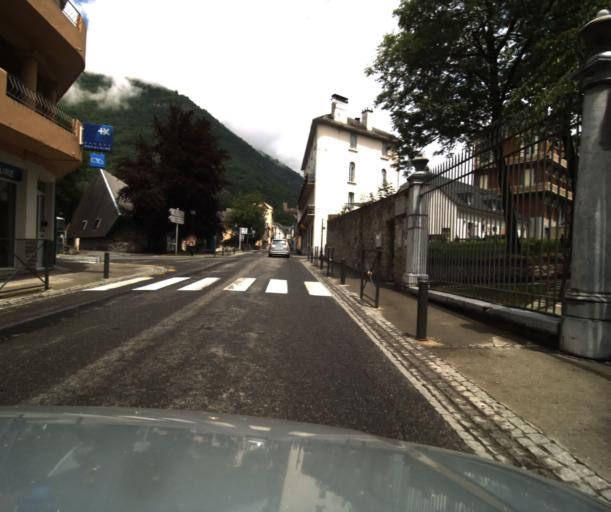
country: FR
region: Midi-Pyrenees
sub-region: Departement des Hautes-Pyrenees
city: Luz-Saint-Sauveur
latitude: 42.8722
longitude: -0.0051
